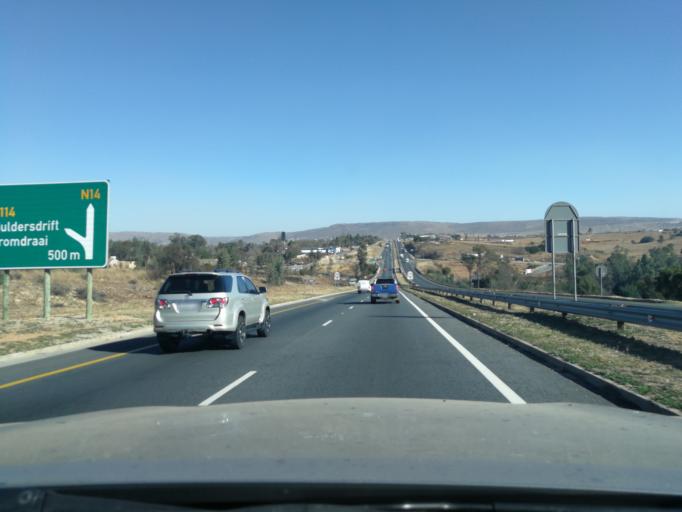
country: ZA
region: Gauteng
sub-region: West Rand District Municipality
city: Muldersdriseloop
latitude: -26.0342
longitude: 27.8469
